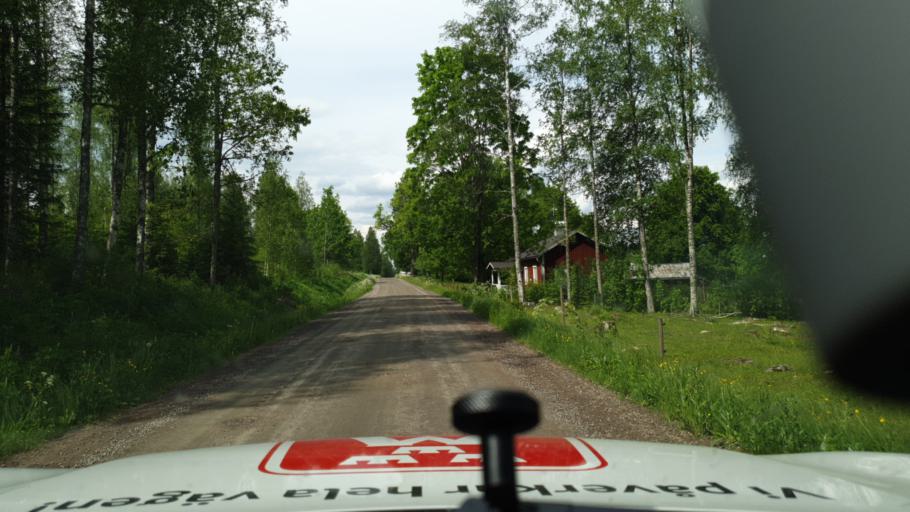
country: SE
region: Vaermland
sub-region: Torsby Kommun
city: Torsby
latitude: 59.9632
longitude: 12.8818
